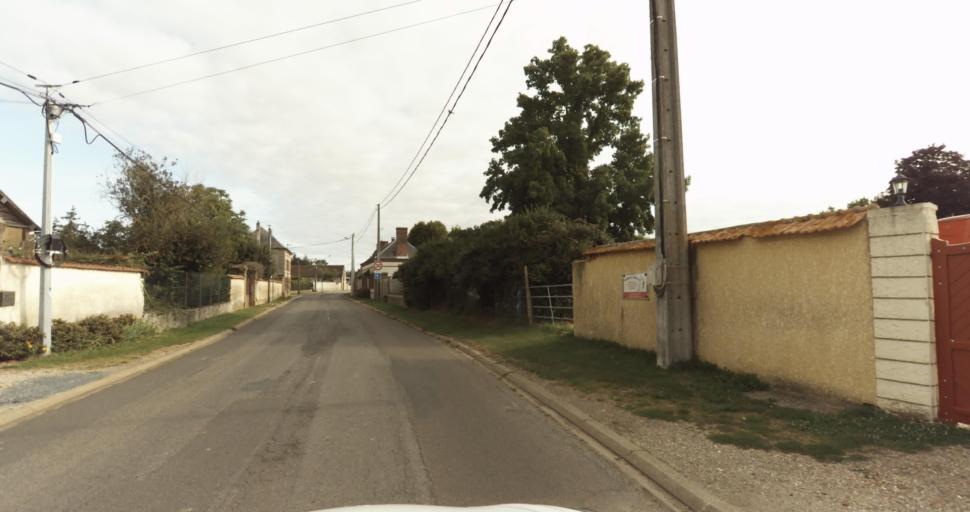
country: FR
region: Haute-Normandie
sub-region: Departement de l'Eure
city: La Madeleine-de-Nonancourt
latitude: 48.8619
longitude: 1.2446
